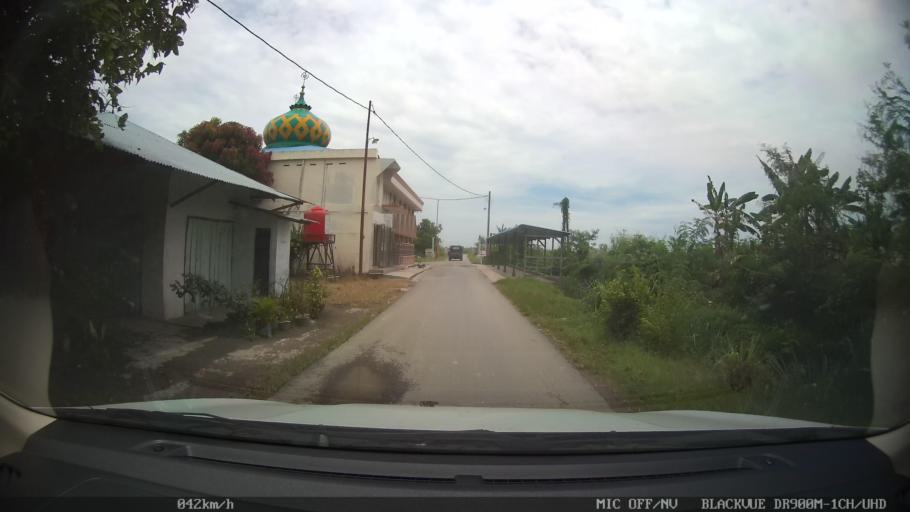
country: ID
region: North Sumatra
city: Sunggal
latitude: 3.6360
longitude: 98.5751
